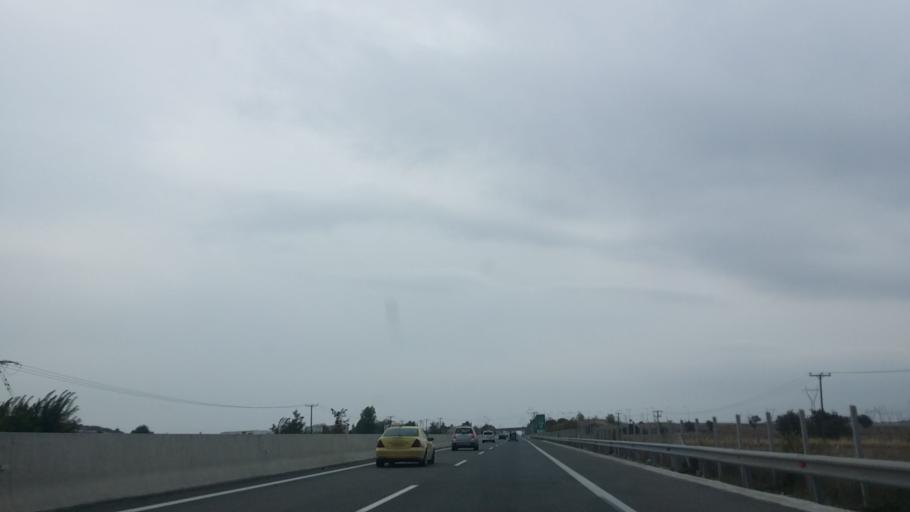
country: GR
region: Central Greece
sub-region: Nomos Voiotias
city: Arma
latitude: 38.3788
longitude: 23.4767
